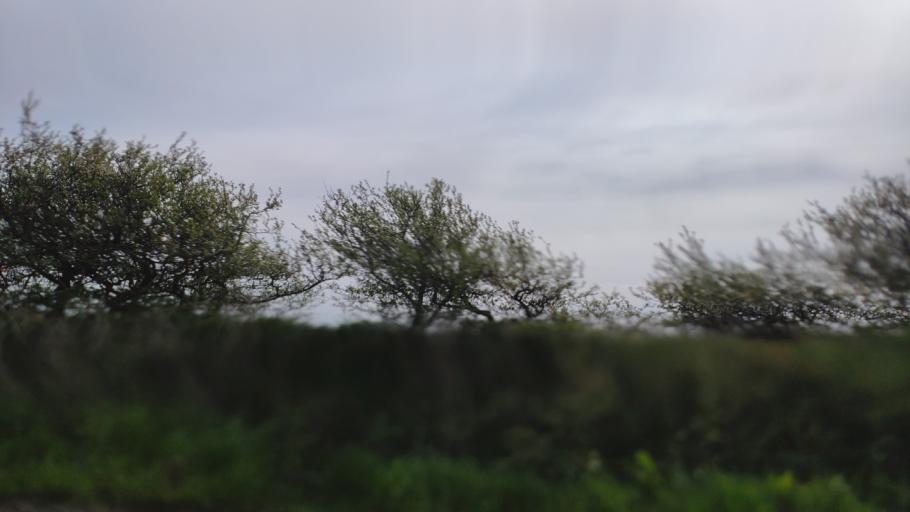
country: IE
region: Munster
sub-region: County Cork
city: Blarney
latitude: 51.9887
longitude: -8.5081
